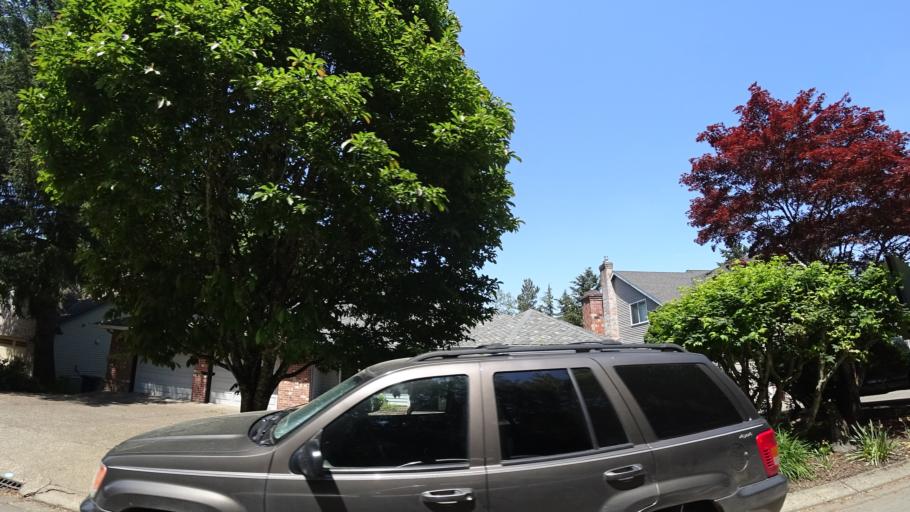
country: US
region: Oregon
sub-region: Washington County
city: Metzger
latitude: 45.4399
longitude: -122.7231
